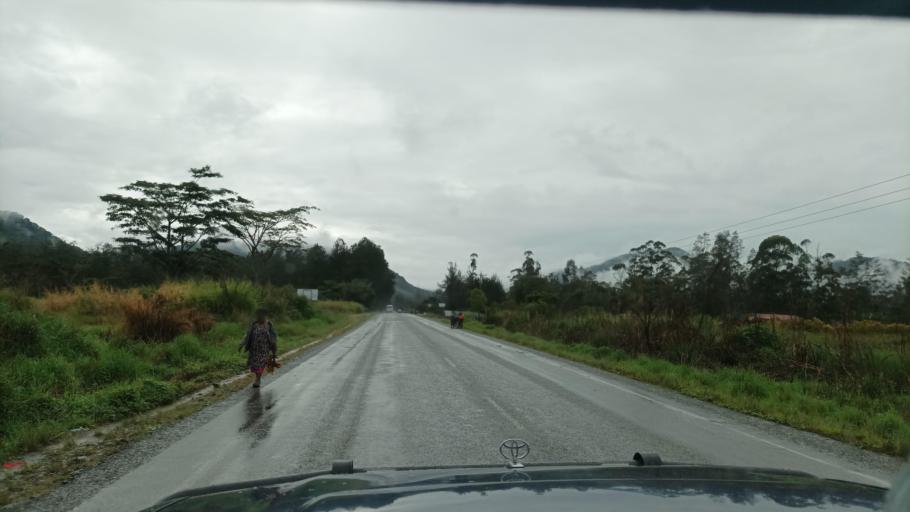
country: PG
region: Western Highlands
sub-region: Hagen
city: Mount Hagen
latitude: -5.8365
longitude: 144.3333
